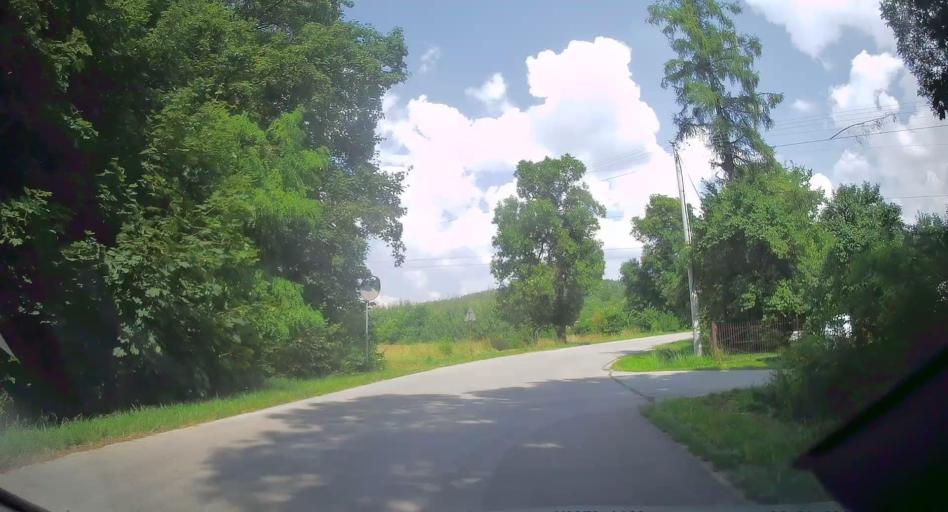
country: PL
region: Swietokrzyskie
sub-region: Powiat kielecki
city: Checiny
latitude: 50.7907
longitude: 20.4507
